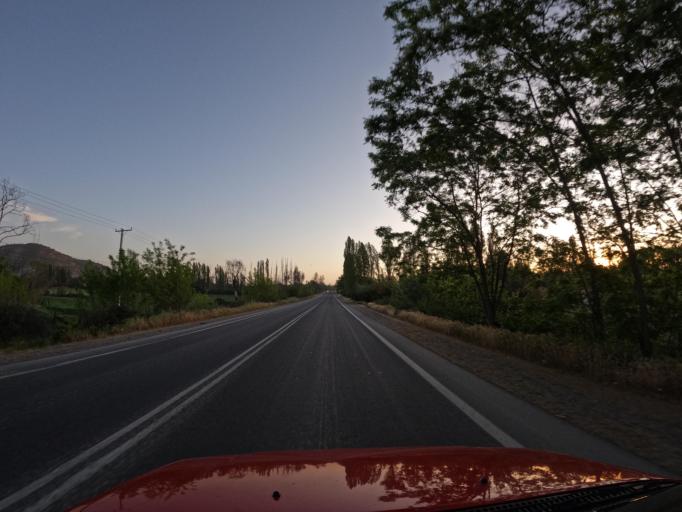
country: CL
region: O'Higgins
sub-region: Provincia de Cachapoal
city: San Vicente
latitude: -34.1627
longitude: -71.3933
